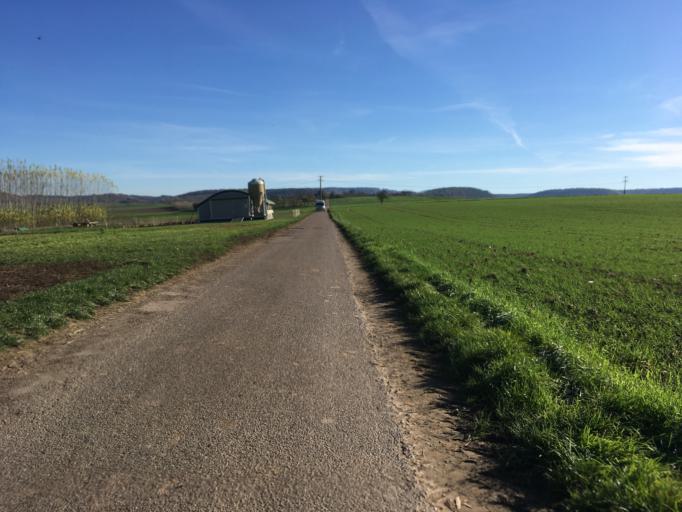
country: DE
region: Baden-Wuerttemberg
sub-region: Karlsruhe Region
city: Oberderdingen
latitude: 49.0772
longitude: 8.7972
